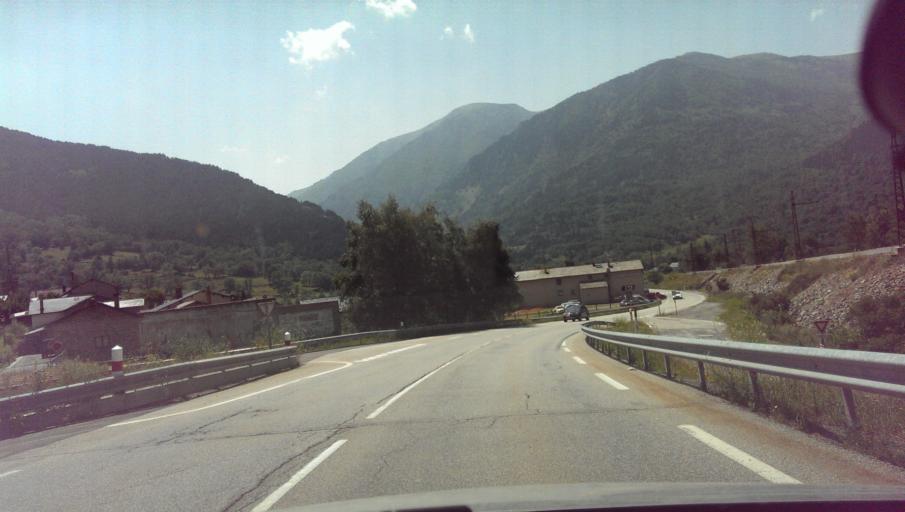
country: ES
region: Catalonia
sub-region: Provincia de Girona
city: Meranges
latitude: 42.5278
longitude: 1.8242
